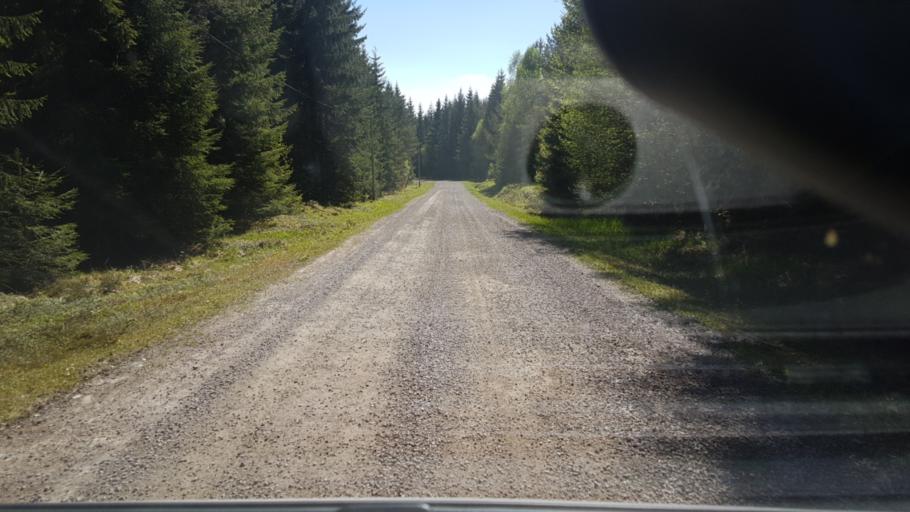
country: SE
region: Vaermland
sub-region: Eda Kommun
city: Charlottenberg
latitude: 59.9035
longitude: 12.3805
